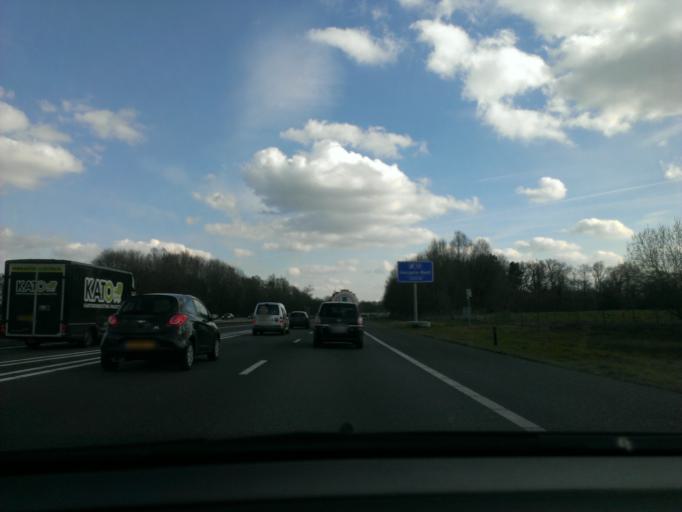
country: NL
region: Overijssel
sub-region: Gemeente Borne
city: Borne
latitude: 52.2820
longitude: 6.7446
